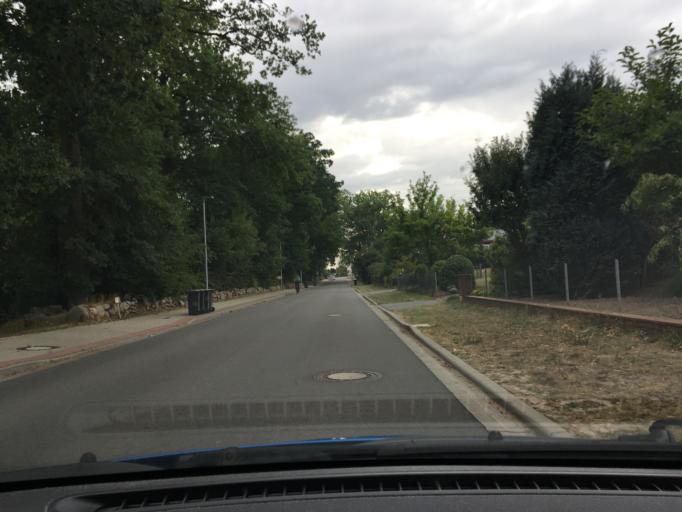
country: DE
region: Lower Saxony
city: Jesteburg
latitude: 53.2701
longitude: 9.9104
